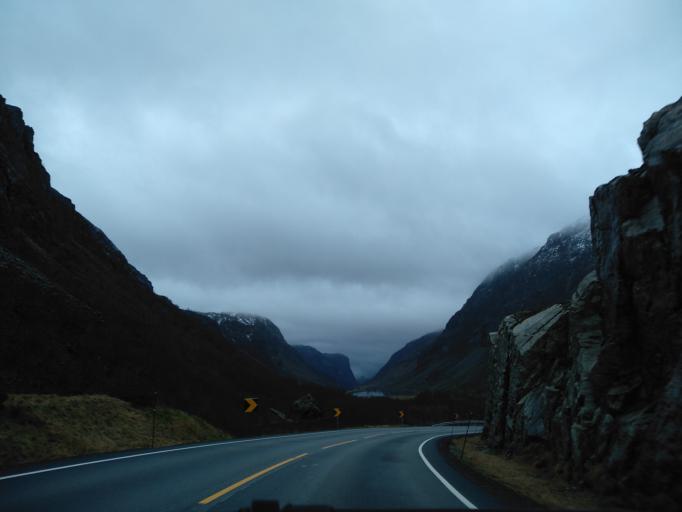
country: NO
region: Vest-Agder
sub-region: Sirdal
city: Tonstad
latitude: 58.8376
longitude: 6.4928
